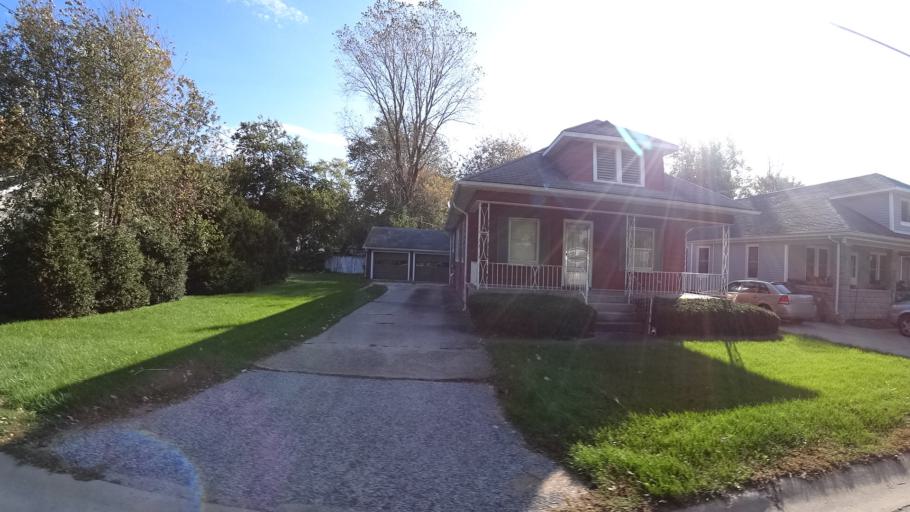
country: US
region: Indiana
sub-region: LaPorte County
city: Trail Creek
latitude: 41.7062
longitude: -86.8647
